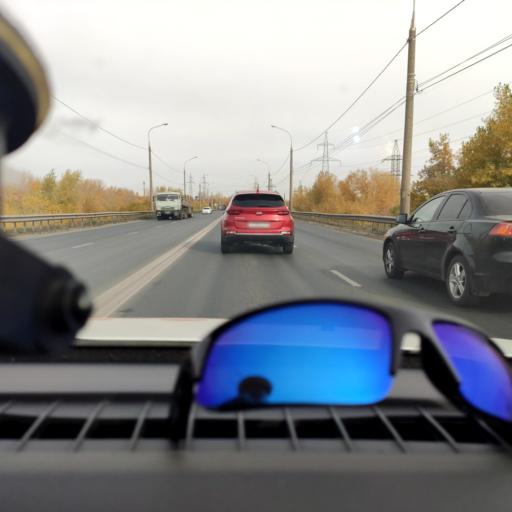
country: RU
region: Samara
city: Samara
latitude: 53.1611
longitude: 50.1940
